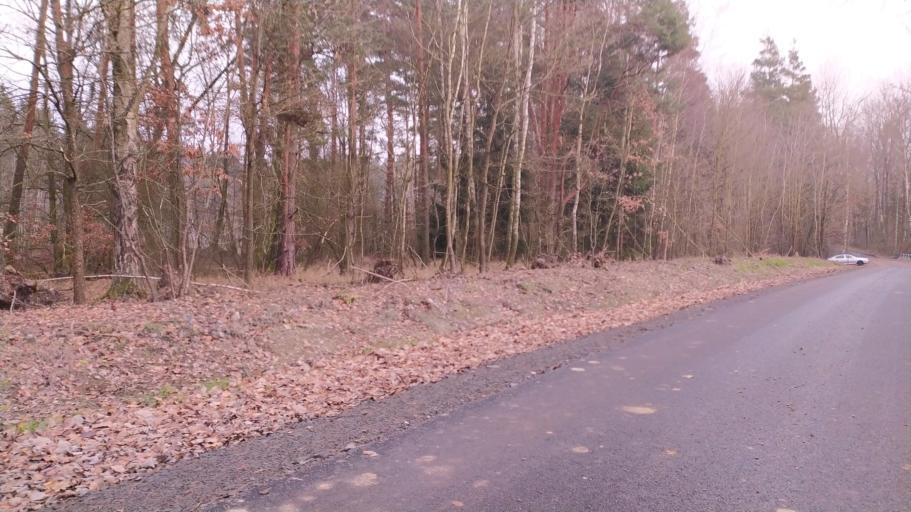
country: DE
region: Bavaria
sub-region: Upper Franconia
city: Schirnding
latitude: 50.0998
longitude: 12.2747
